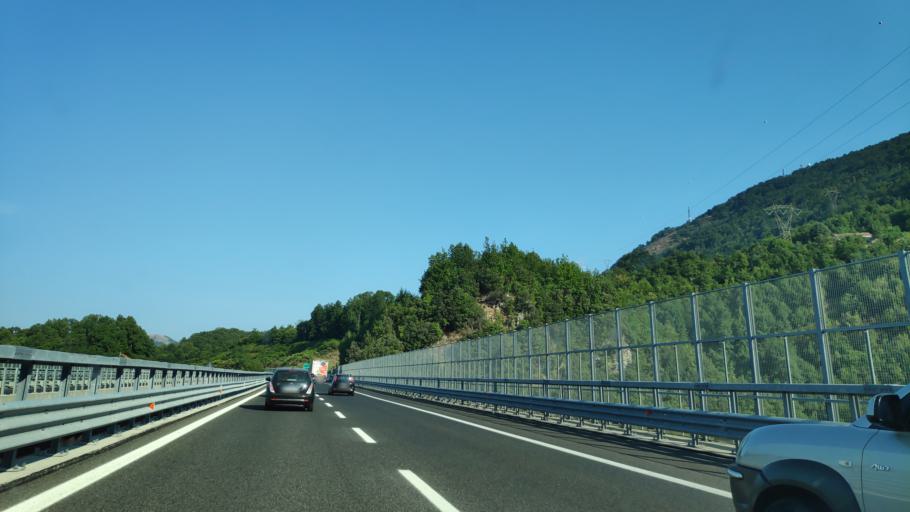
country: IT
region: Basilicate
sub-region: Provincia di Potenza
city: Lagonegro
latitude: 40.1273
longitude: 15.7760
